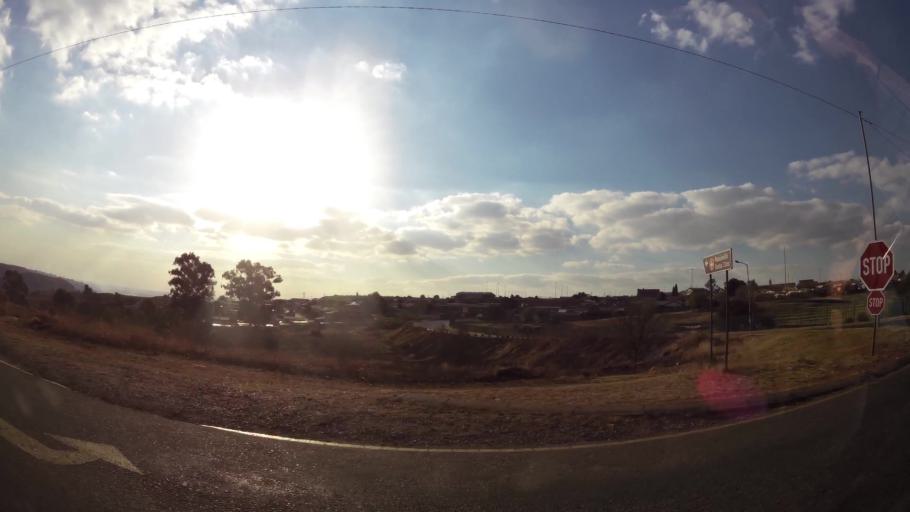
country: ZA
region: Gauteng
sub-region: West Rand District Municipality
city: Krugersdorp
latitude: -26.0837
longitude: 27.7539
